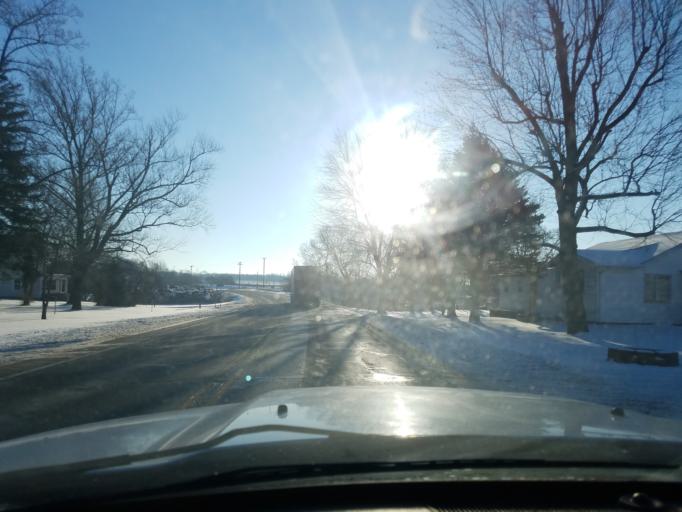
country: US
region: Indiana
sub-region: Noble County
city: Rome City
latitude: 41.4538
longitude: -85.3972
